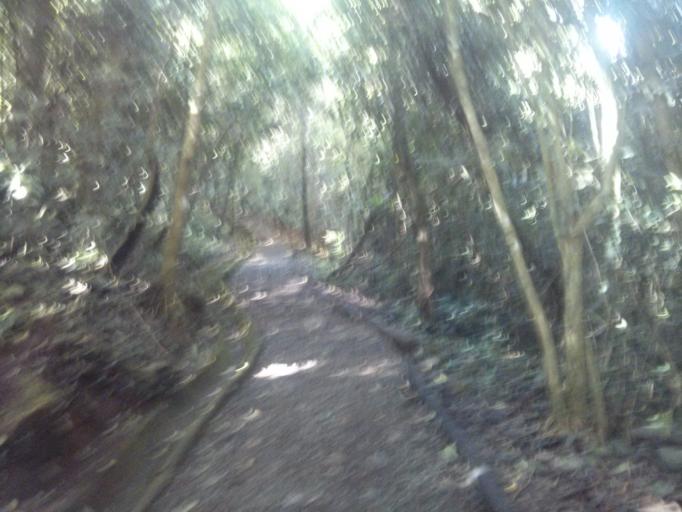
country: CR
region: Cartago
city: Turrialba
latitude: 9.9716
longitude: -83.6915
